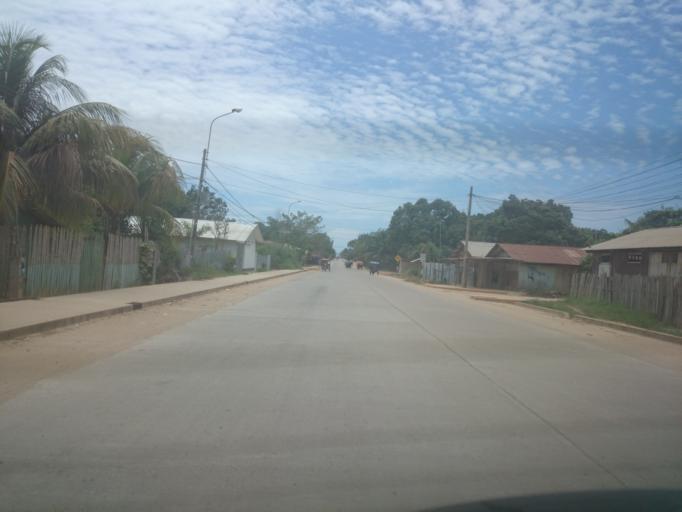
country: PE
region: Ucayali
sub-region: Provincia de Coronel Portillo
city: Puerto Callao
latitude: -8.3667
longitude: -74.5747
